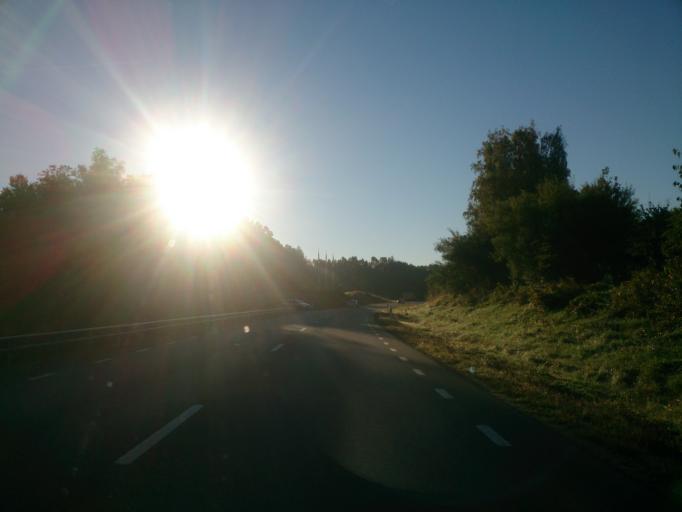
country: SE
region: OEstergoetland
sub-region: Atvidabergs Kommun
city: Atvidaberg
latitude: 58.1962
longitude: 16.0169
